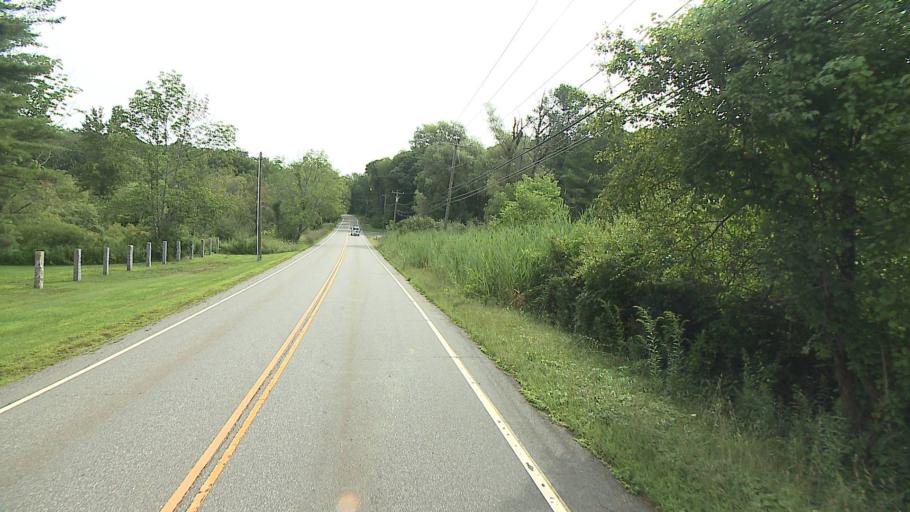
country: US
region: Connecticut
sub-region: Litchfield County
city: Kent
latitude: 41.7150
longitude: -73.4347
